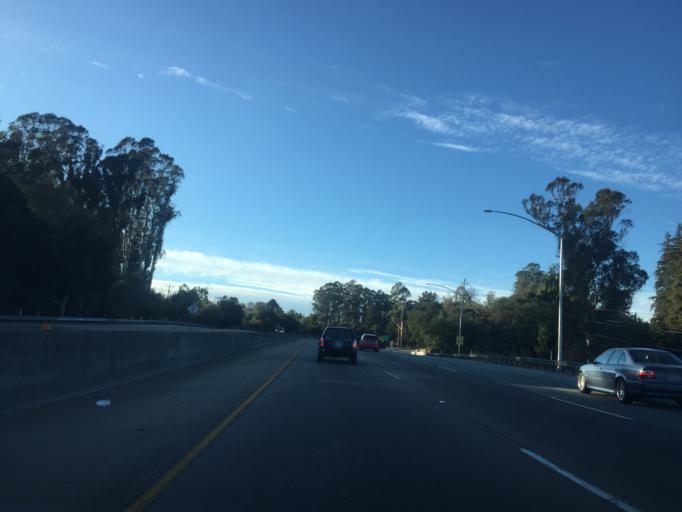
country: US
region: California
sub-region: Santa Cruz County
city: Pasatiempo
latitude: 36.9959
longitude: -122.0197
